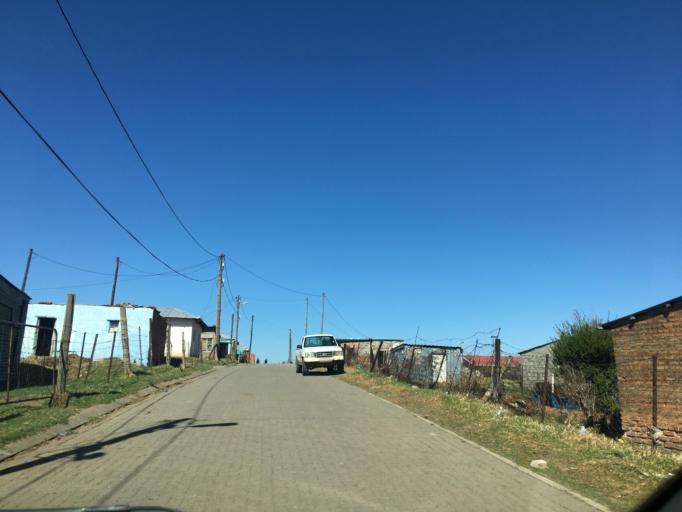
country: ZA
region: Eastern Cape
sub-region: Chris Hani District Municipality
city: Elliot
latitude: -31.3379
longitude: 27.8601
